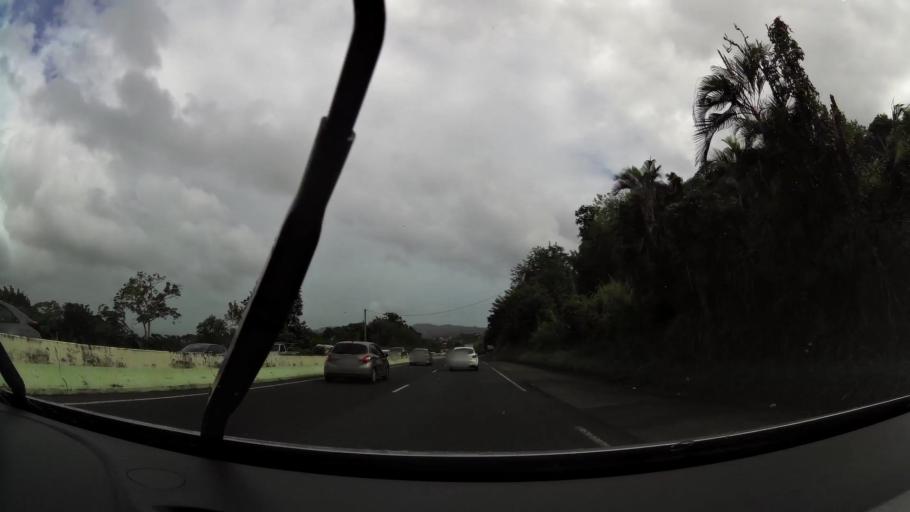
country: MQ
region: Martinique
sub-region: Martinique
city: Ducos
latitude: 14.5786
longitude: -60.9831
